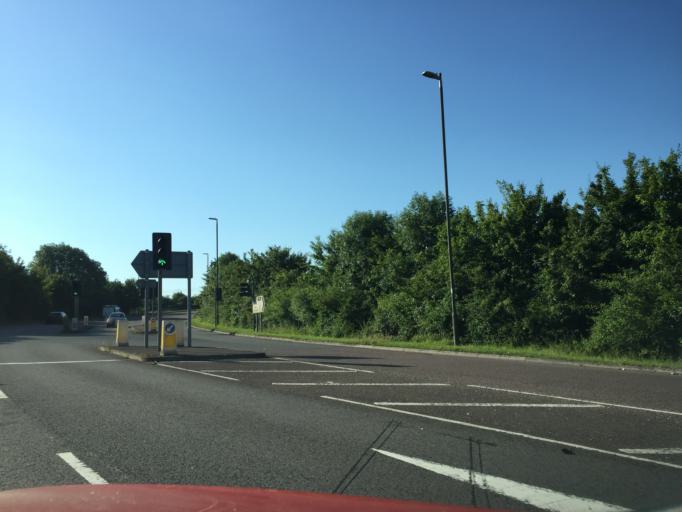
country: GB
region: England
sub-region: South Gloucestershire
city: Siston
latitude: 51.4706
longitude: -2.4795
